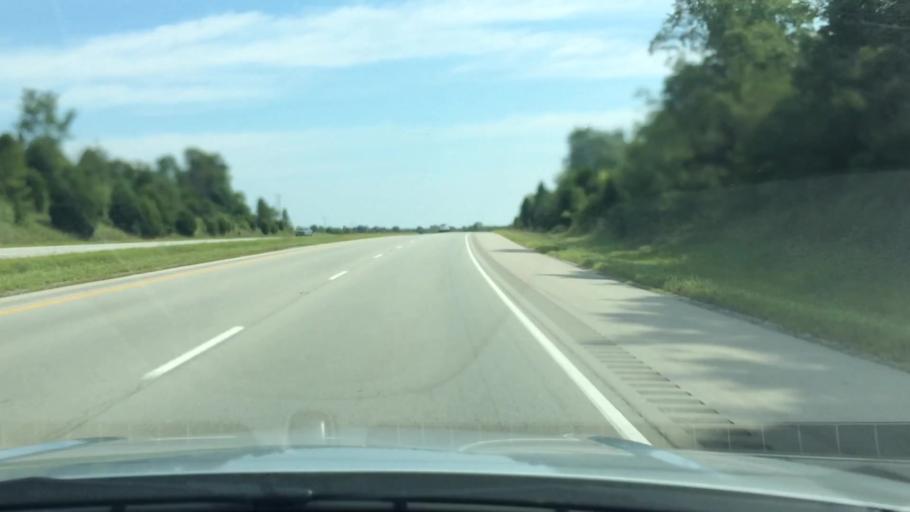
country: US
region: Kentucky
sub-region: Franklin County
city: Frankfort
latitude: 38.1347
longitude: -84.9101
